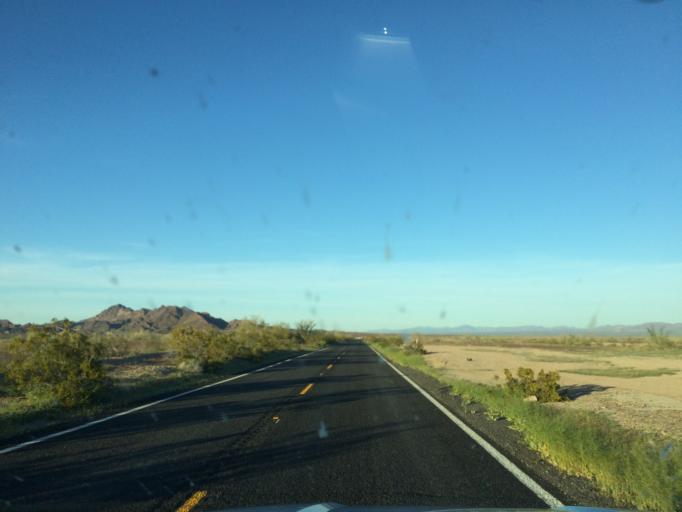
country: US
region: California
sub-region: Riverside County
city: Mesa Verde
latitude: 33.2637
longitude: -114.8031
